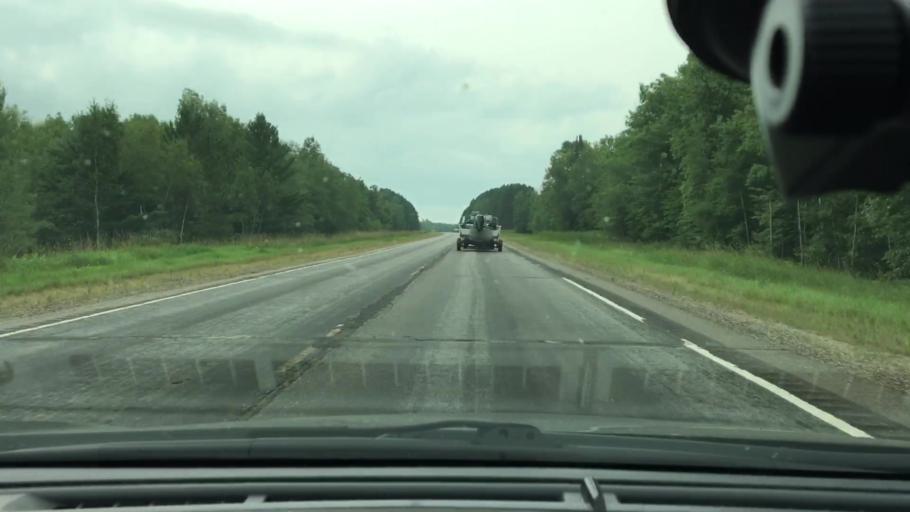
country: US
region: Minnesota
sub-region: Crow Wing County
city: Crosby
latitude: 46.6396
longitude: -93.9503
